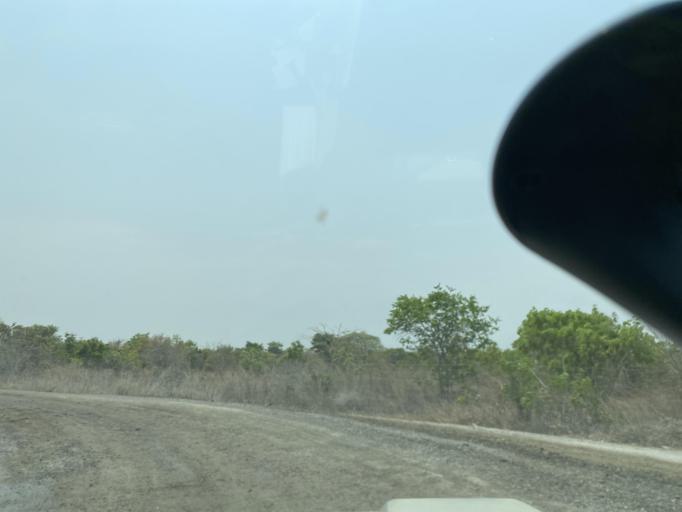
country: ZM
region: Lusaka
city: Lusaka
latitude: -15.5369
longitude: 28.4486
